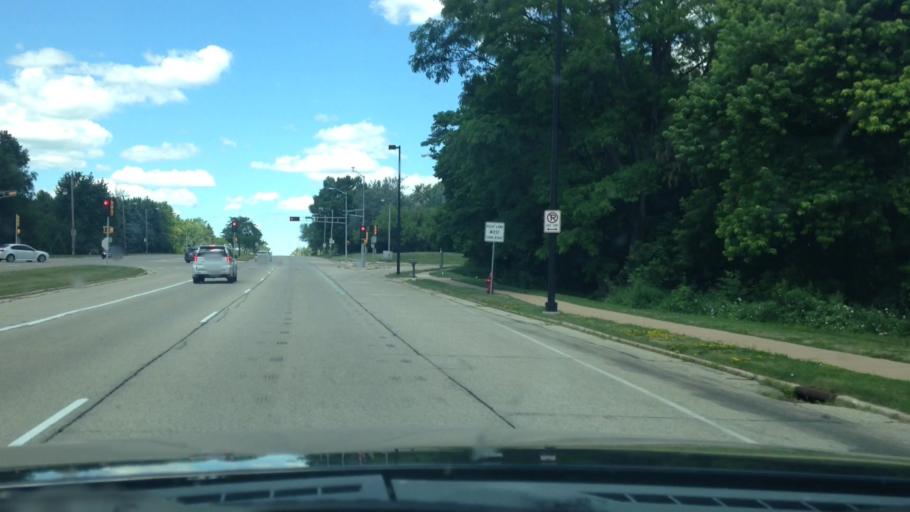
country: US
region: Wisconsin
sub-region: Waukesha County
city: Menomonee Falls
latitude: 43.1550
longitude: -88.0834
